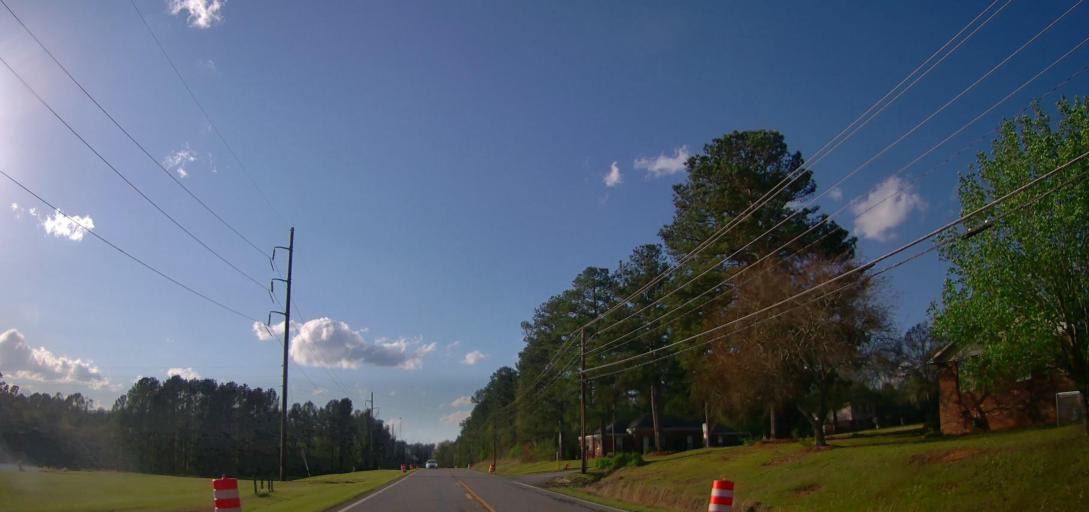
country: US
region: Georgia
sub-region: Baldwin County
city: Milledgeville
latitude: 33.0984
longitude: -83.2692
